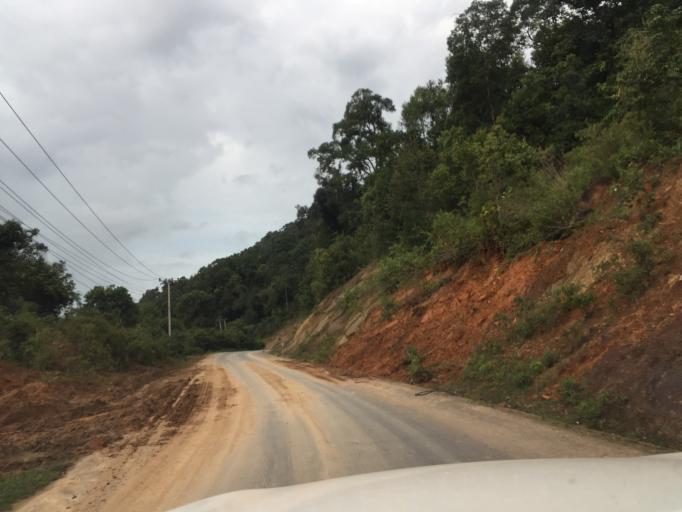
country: LA
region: Phongsali
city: Phongsali
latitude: 21.3154
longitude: 102.0485
